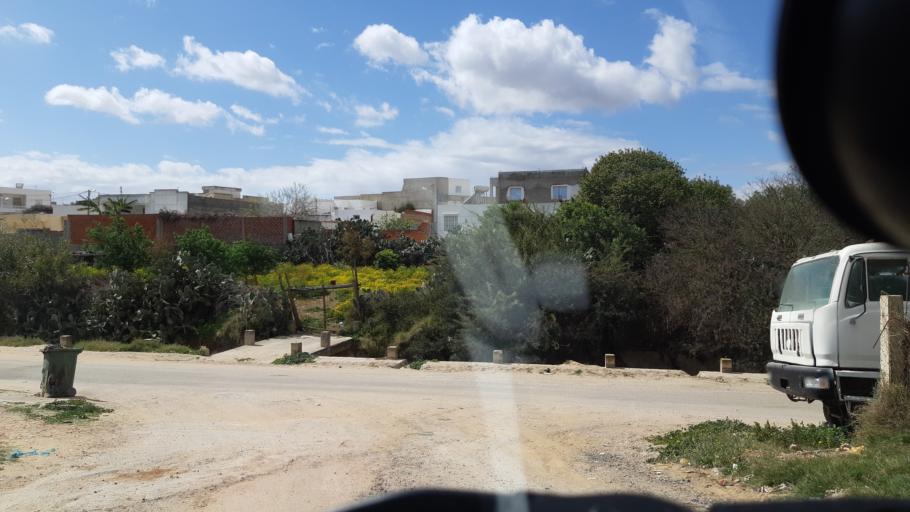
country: TN
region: Susah
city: Akouda
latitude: 35.8789
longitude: 10.5334
